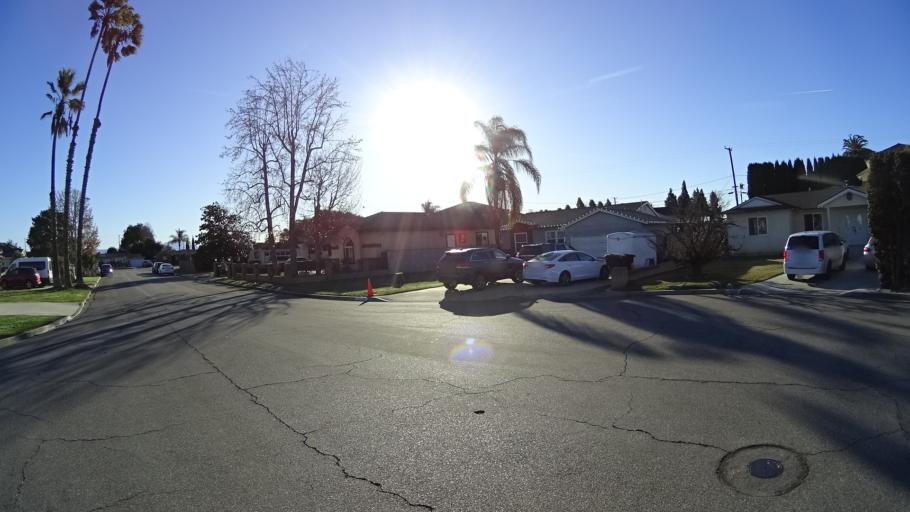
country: US
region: California
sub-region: Orange County
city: Garden Grove
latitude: 33.7681
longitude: -117.9697
